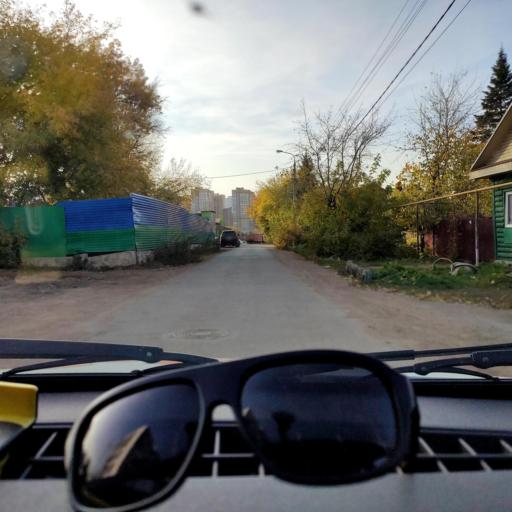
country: RU
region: Bashkortostan
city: Ufa
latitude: 54.7213
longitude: 55.9721
